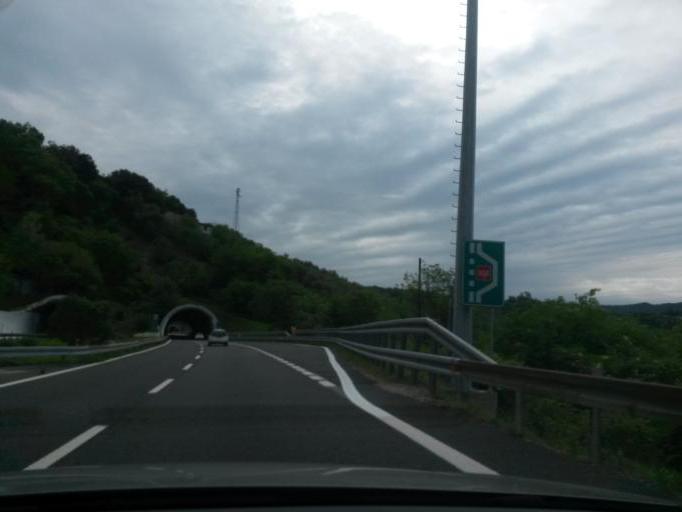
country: IT
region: Liguria
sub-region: Provincia di Genova
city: Moneglia
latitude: 44.2546
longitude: 9.4913
